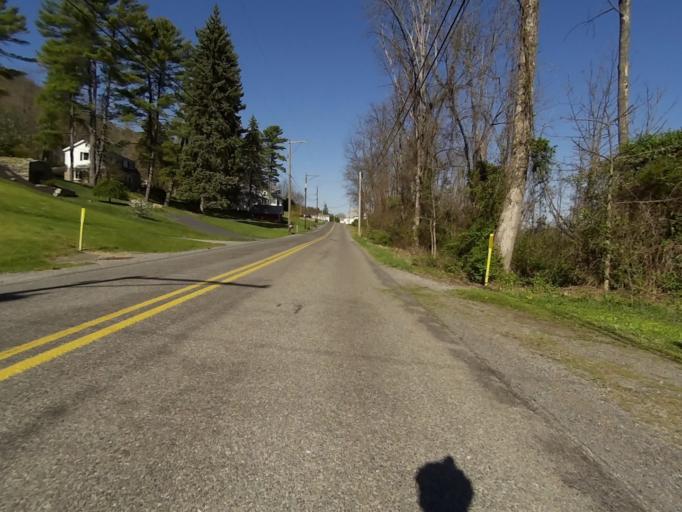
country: US
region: Pennsylvania
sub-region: Centre County
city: Bellefonte
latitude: 40.8977
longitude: -77.8336
